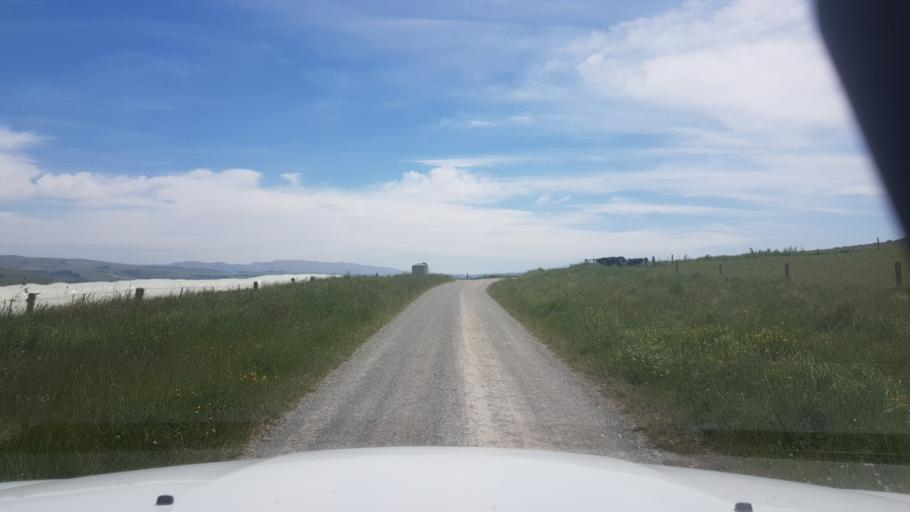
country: NZ
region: Canterbury
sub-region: Timaru District
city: Pleasant Point
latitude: -44.1703
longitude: 171.0190
